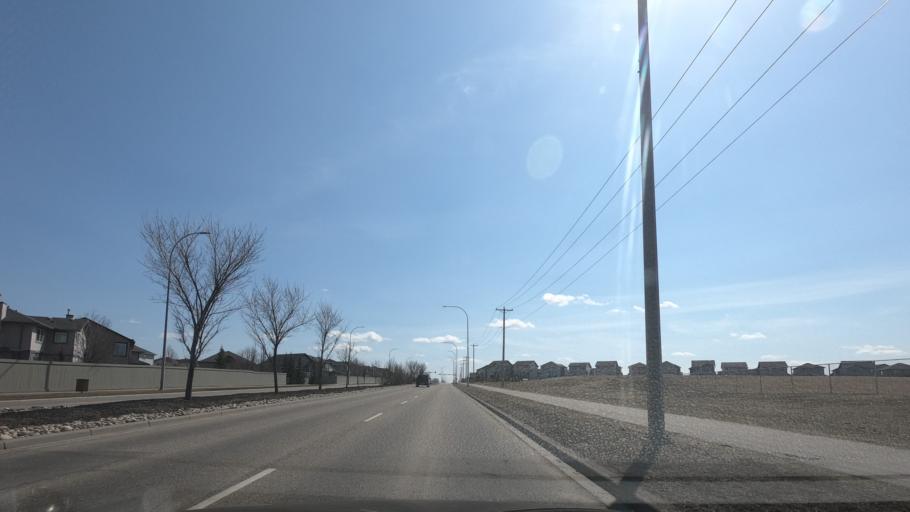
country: CA
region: Alberta
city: Airdrie
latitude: 51.2691
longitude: -114.0252
